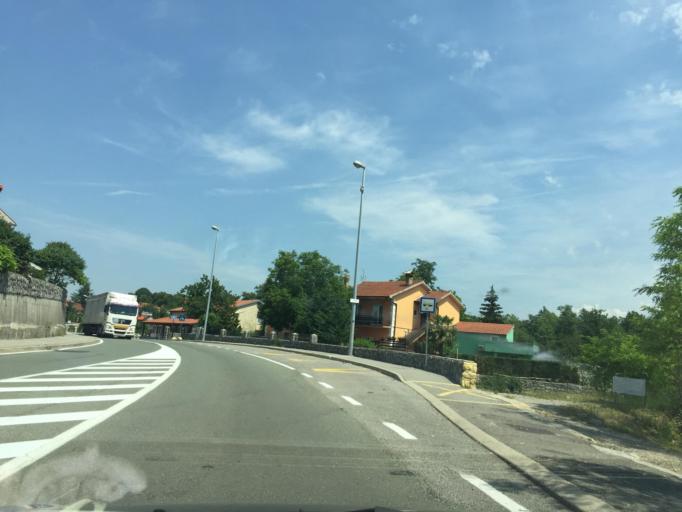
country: HR
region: Primorsko-Goranska
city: Matulji
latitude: 45.3991
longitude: 14.3084
